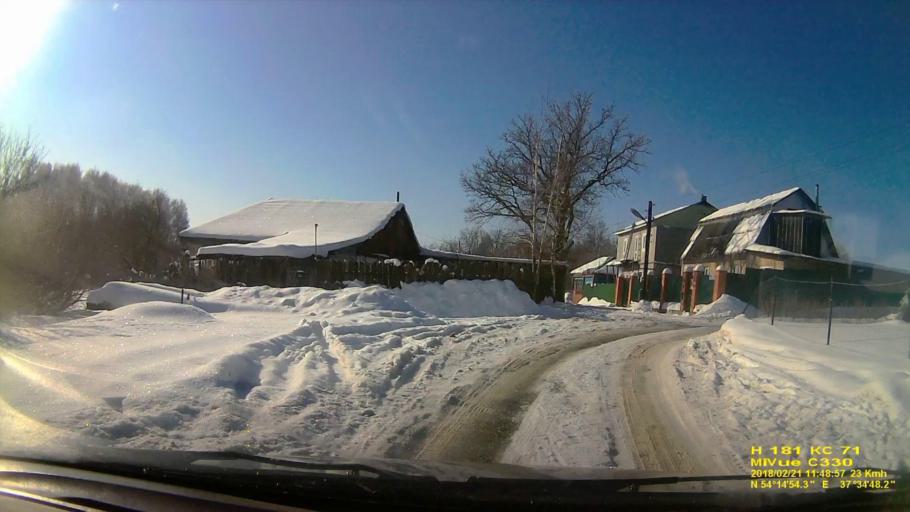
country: RU
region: Tula
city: Gorelki
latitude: 54.2486
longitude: 37.5803
